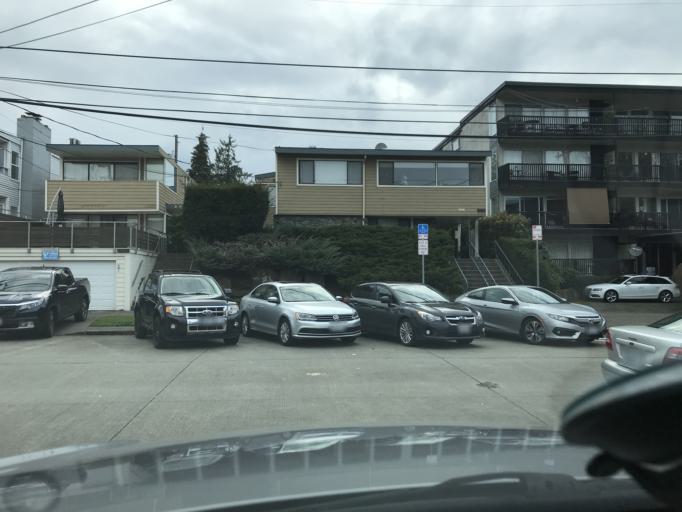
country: US
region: Washington
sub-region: King County
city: Medina
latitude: 47.6379
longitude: -122.2770
